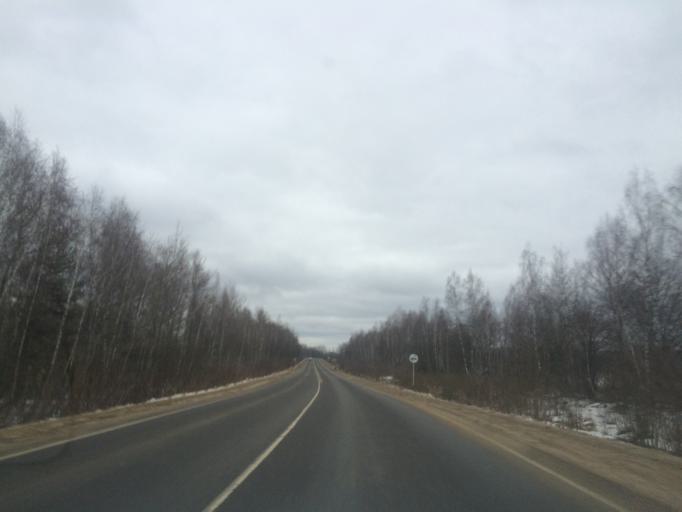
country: RU
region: Tula
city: Odoyev
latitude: 54.0010
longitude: 36.7613
